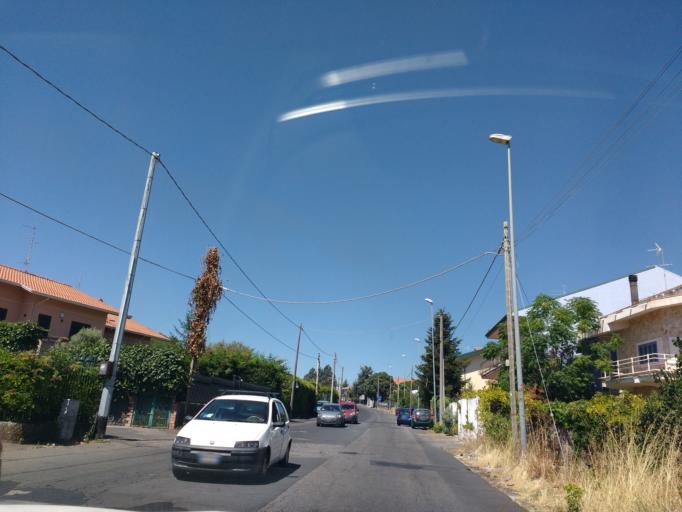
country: IT
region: Sicily
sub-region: Catania
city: Nicolosi
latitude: 37.6098
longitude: 15.0255
